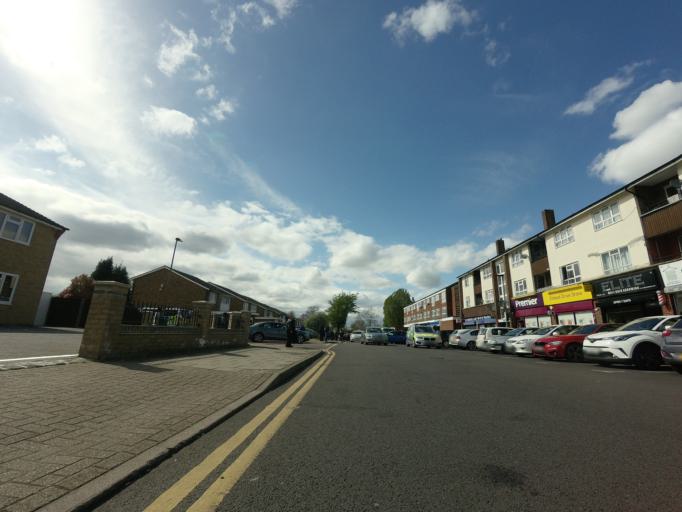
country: GB
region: England
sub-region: Greater London
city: Orpington
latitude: 51.3738
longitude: 0.1171
